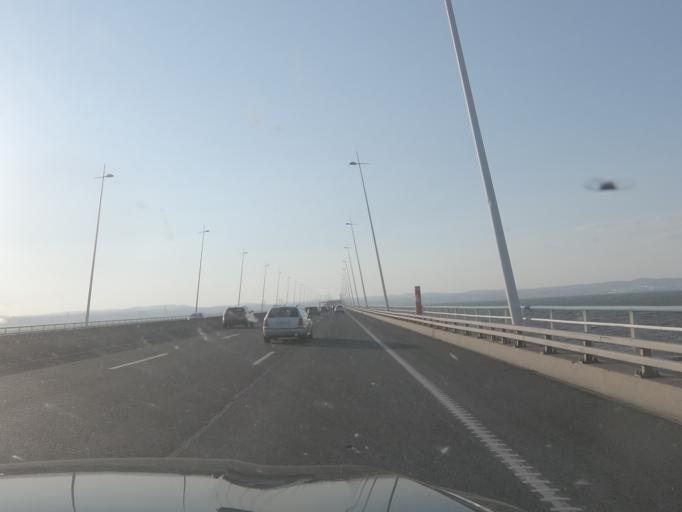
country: PT
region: Setubal
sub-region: Montijo
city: Montijo
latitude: 38.7437
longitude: -9.0199
